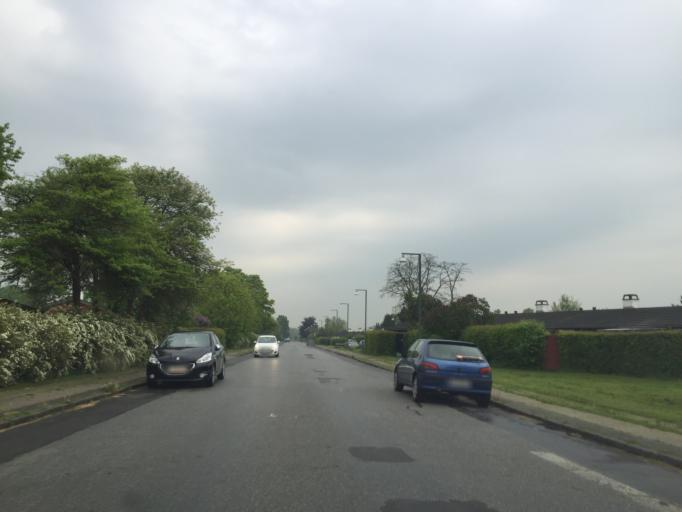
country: DK
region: Capital Region
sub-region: Rodovre Kommune
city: Rodovre
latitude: 55.6814
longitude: 12.4361
